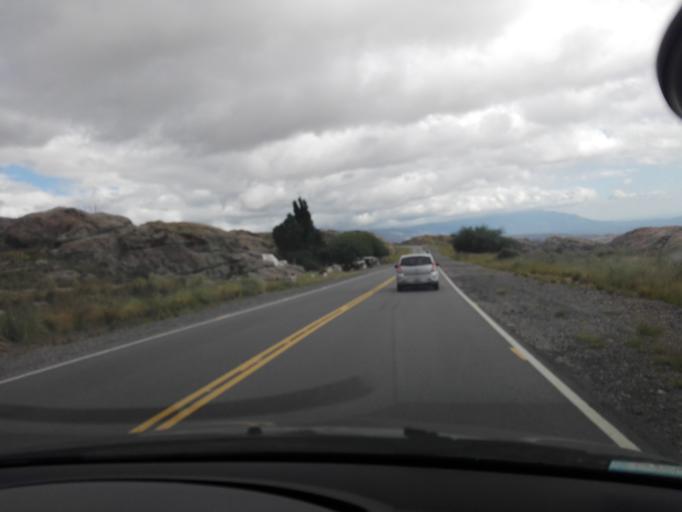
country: AR
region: Cordoba
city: Mina Clavero
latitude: -31.6342
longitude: -64.9082
